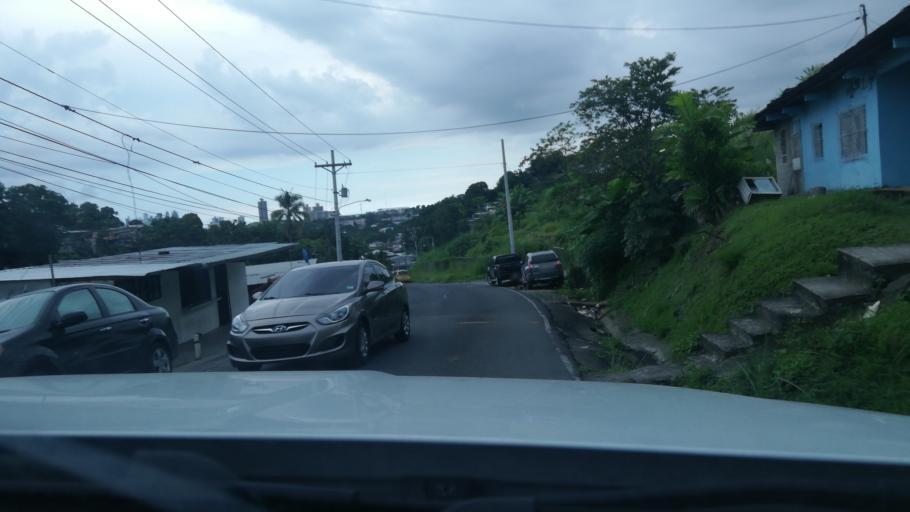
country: PA
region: Panama
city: San Miguelito
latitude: 9.0494
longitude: -79.4929
